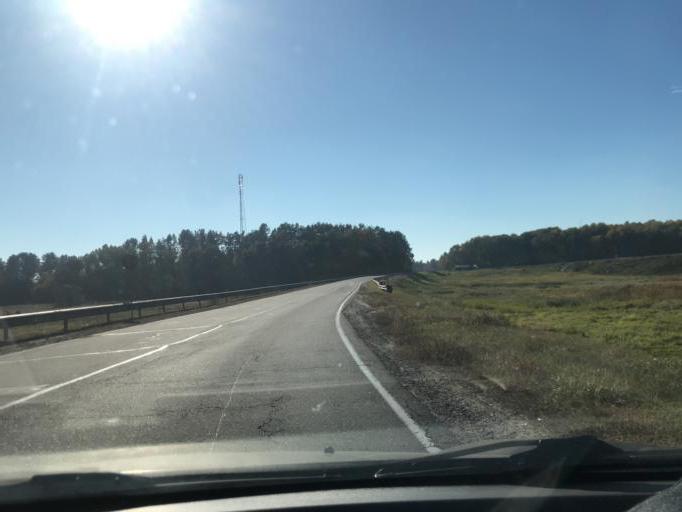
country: BY
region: Gomel
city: Gomel
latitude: 52.3871
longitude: 30.8318
